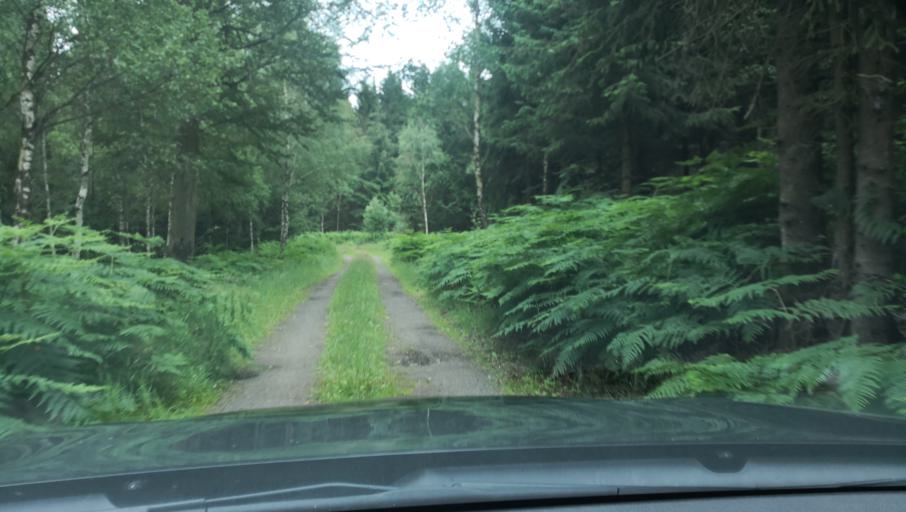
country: SE
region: Skane
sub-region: Simrishamns Kommun
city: Kivik
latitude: 55.6131
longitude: 14.1174
